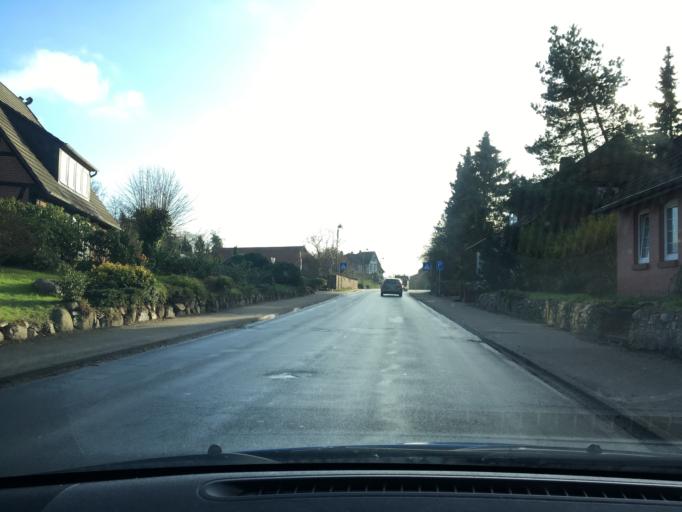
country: DE
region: Lower Saxony
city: Scharnebeck
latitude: 53.2890
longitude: 10.5038
